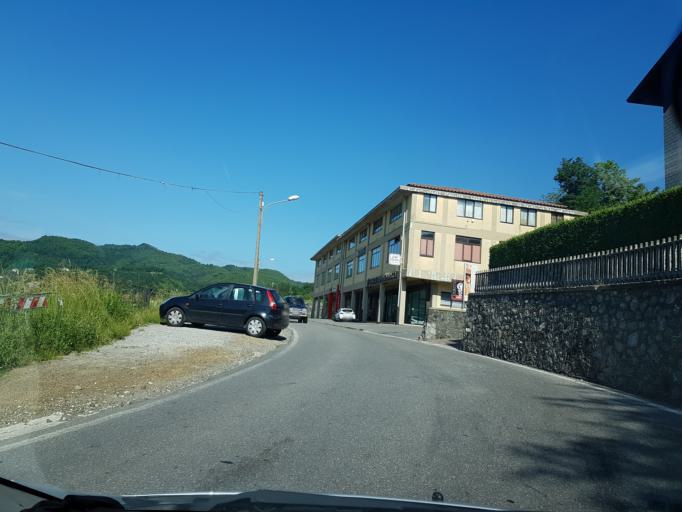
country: IT
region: Tuscany
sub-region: Provincia di Lucca
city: Piazza al Serchio-San Michele
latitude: 44.1849
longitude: 10.2982
